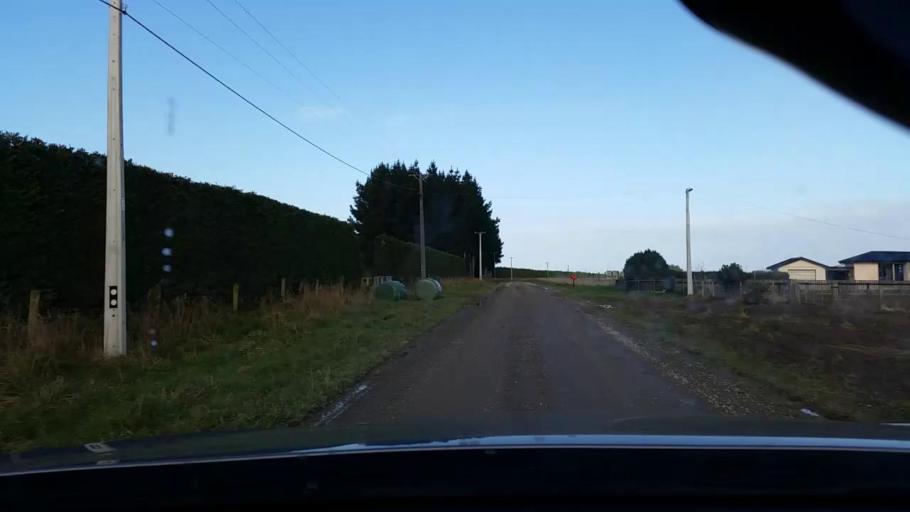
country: NZ
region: Southland
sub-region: Invercargill City
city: Invercargill
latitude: -46.2803
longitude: 168.2940
